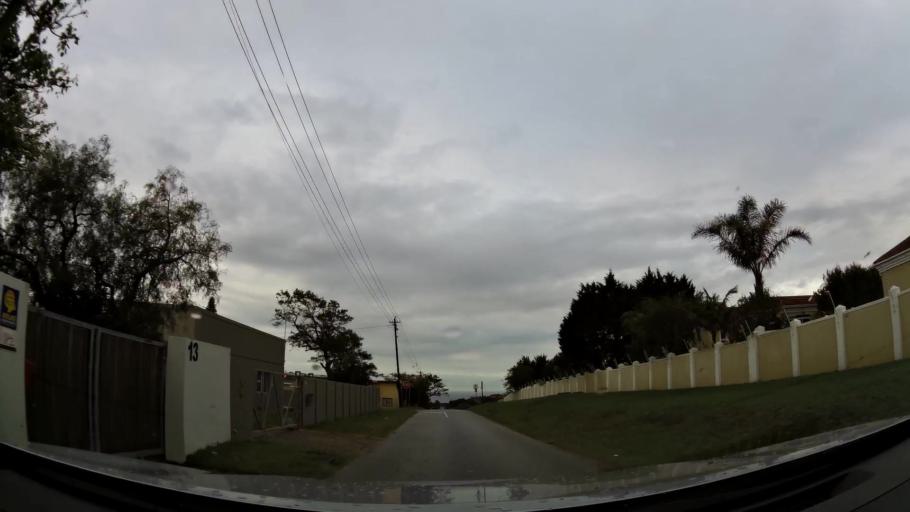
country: ZA
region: Eastern Cape
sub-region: Nelson Mandela Bay Metropolitan Municipality
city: Port Elizabeth
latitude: -33.9984
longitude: 25.5285
